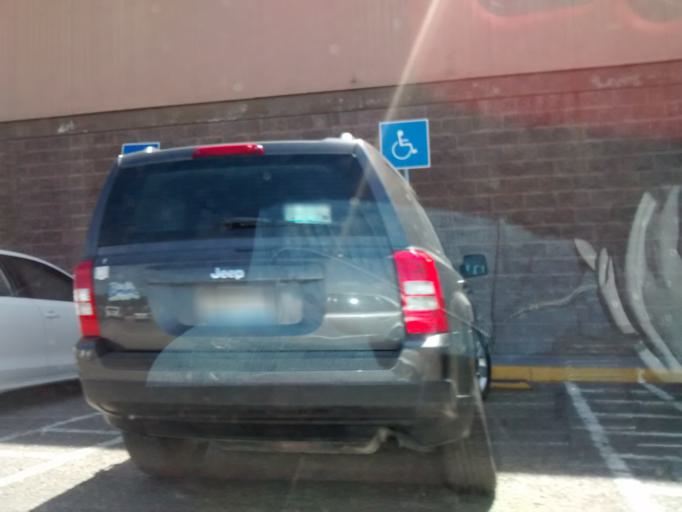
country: MX
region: Puebla
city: Tehuacan
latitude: 18.4678
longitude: -97.4158
